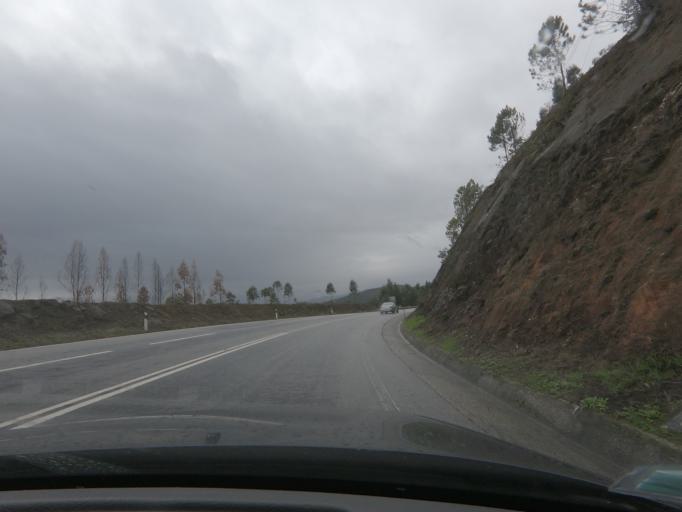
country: PT
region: Braga
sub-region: Celorico de Basto
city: Celorico de Basto
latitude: 41.3453
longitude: -8.0265
